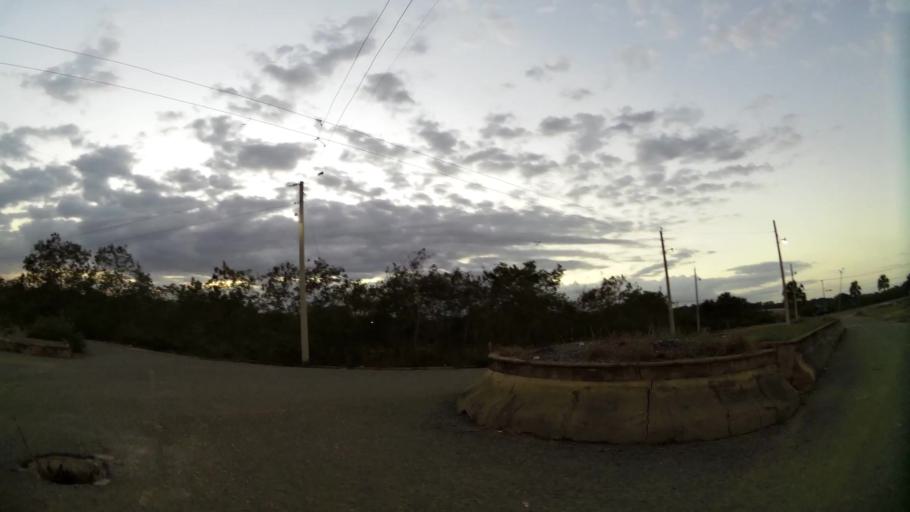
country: DO
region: Nacional
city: La Agustina
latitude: 18.5480
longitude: -69.9493
